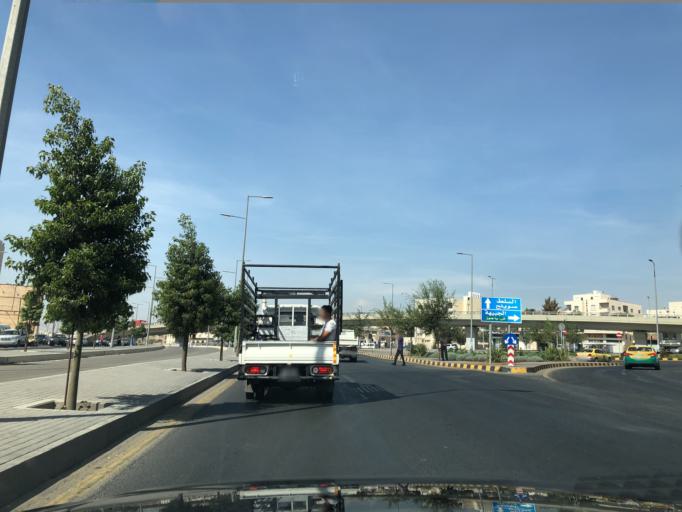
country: JO
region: Amman
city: Al Jubayhah
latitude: 32.0248
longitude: 35.8562
